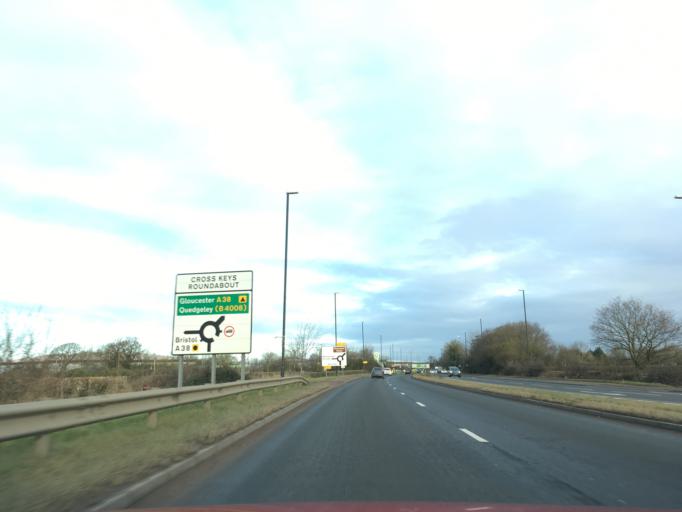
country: GB
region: England
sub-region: Gloucestershire
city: Stonehouse
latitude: 51.8026
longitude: -2.2897
